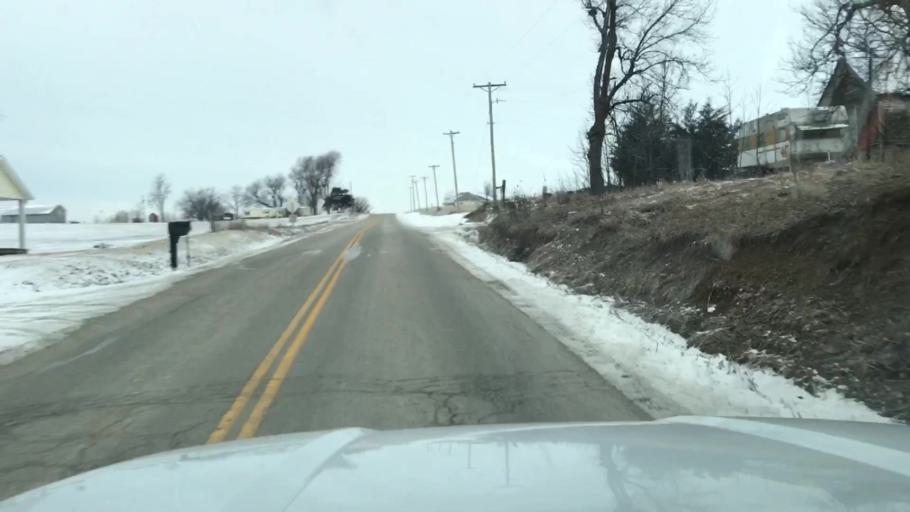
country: US
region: Missouri
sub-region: Andrew County
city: Savannah
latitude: 40.0247
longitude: -94.9211
